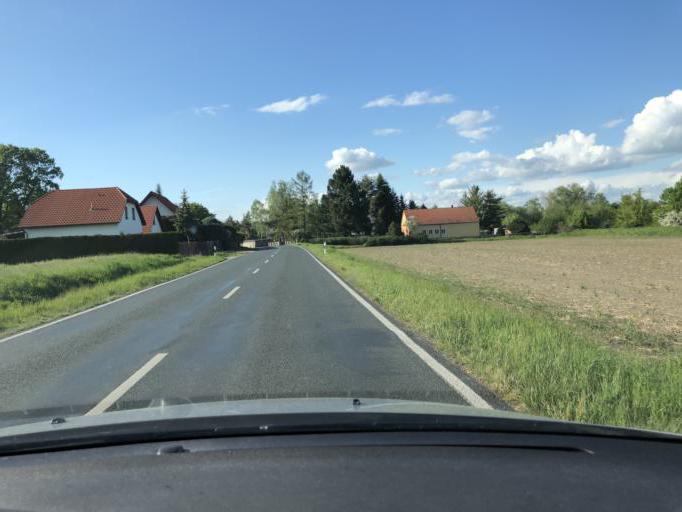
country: DE
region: Saxony
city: Deutzen
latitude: 51.1081
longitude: 12.4282
